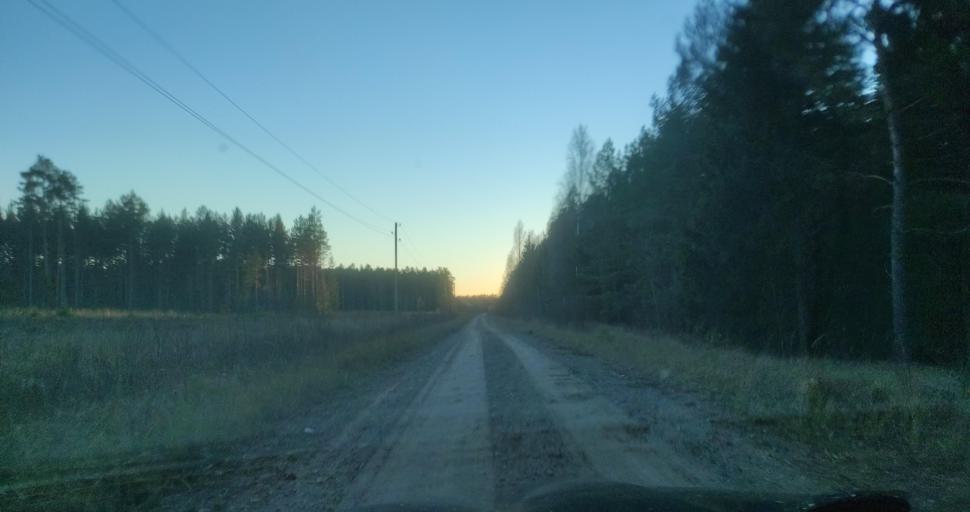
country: LV
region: Dundaga
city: Dundaga
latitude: 57.3723
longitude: 22.0766
